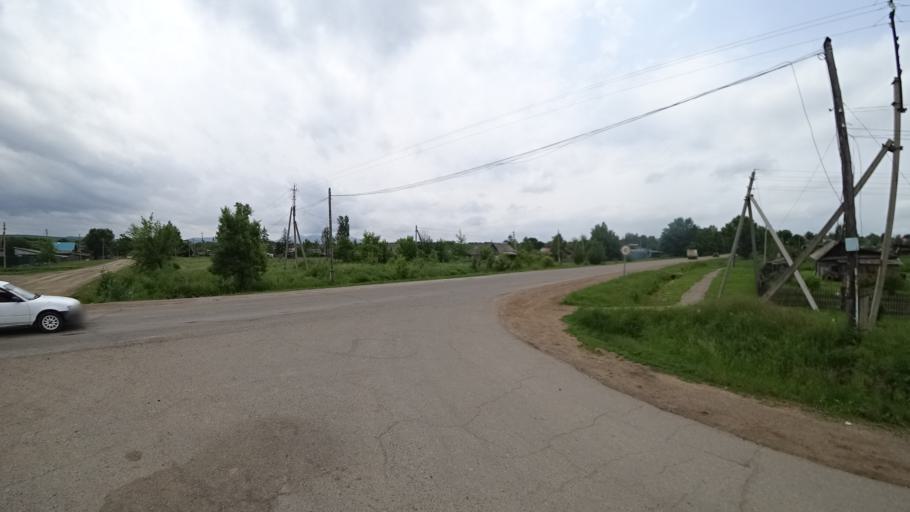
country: RU
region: Primorskiy
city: Novosysoyevka
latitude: 44.2314
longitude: 133.3715
